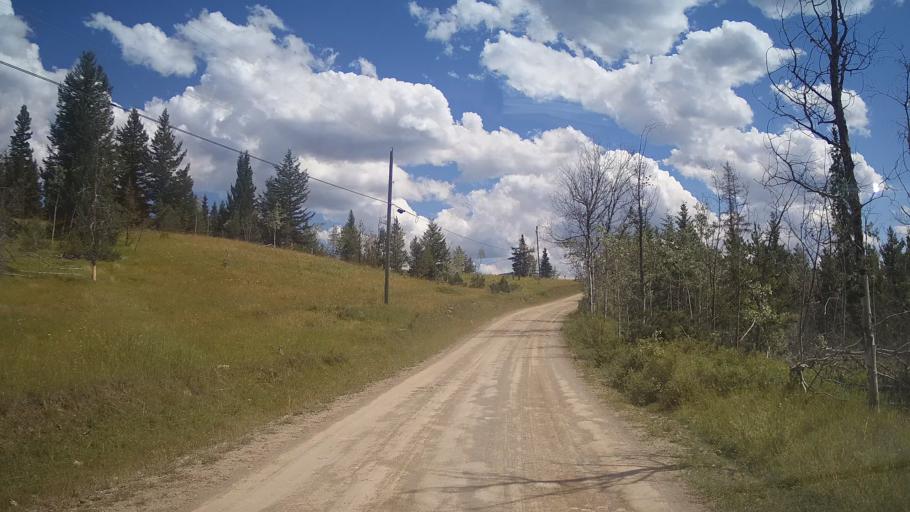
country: CA
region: British Columbia
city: Lillooet
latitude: 51.2888
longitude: -121.9742
